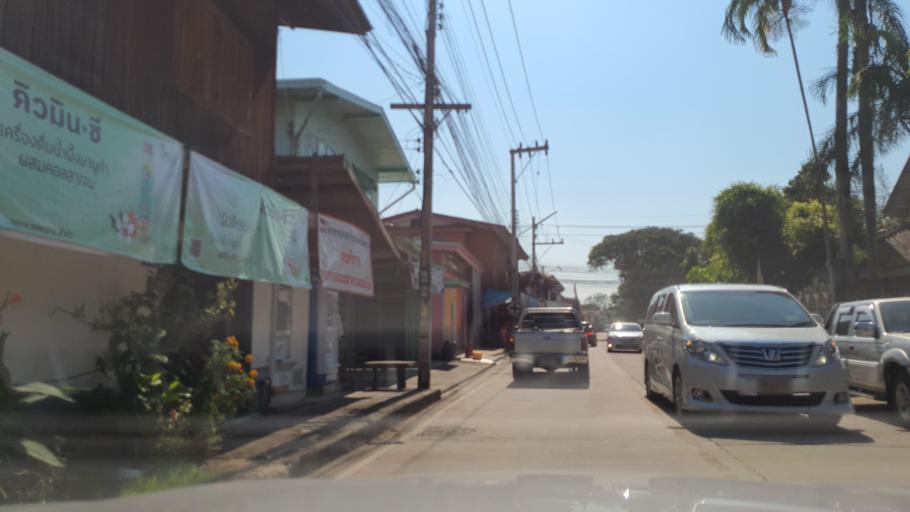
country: TH
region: Nan
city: Nan
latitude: 18.7739
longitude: 100.7681
